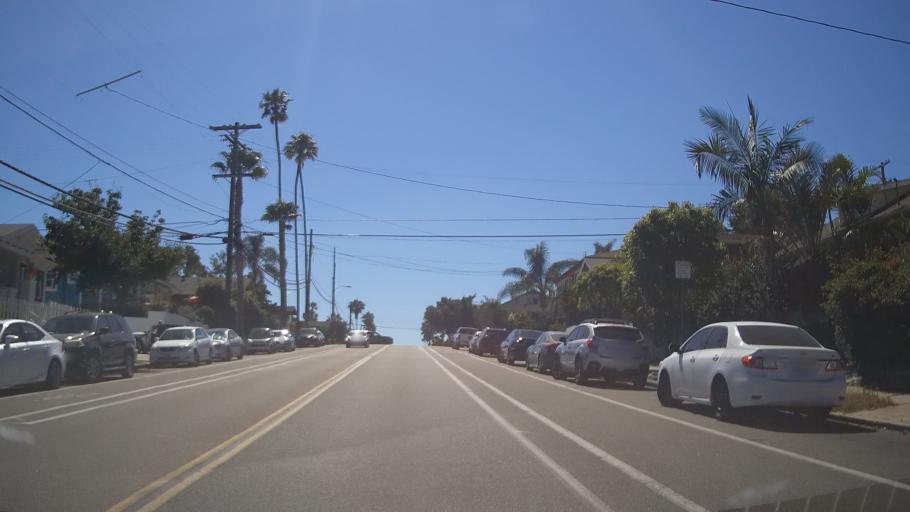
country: US
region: California
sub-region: San Diego County
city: San Diego
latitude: 32.7610
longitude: -117.1439
